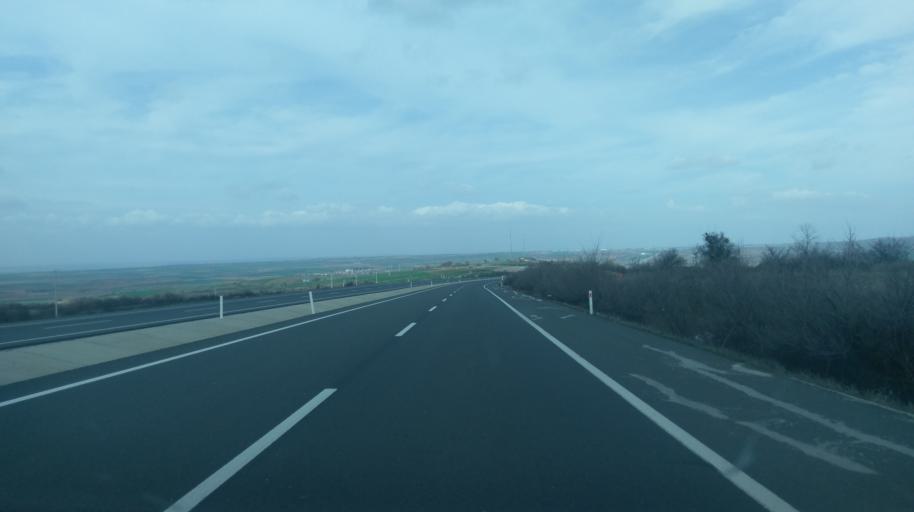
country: TR
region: Edirne
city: Hamidiye
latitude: 41.0856
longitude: 26.6399
